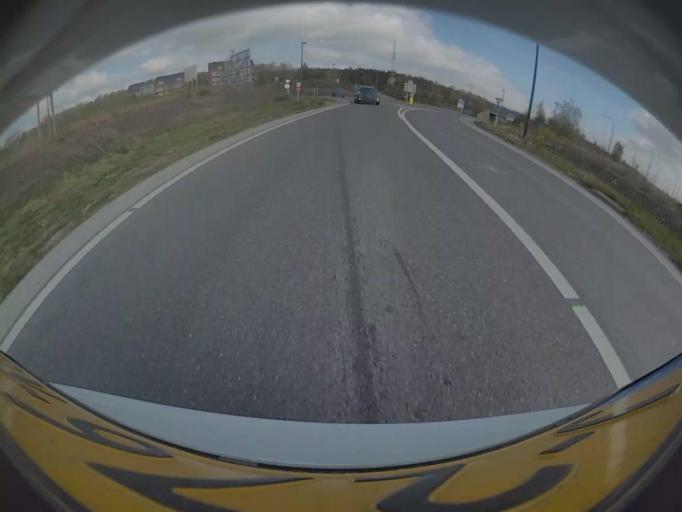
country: BE
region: Wallonia
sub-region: Province du Luxembourg
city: Marche-en-Famenne
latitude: 50.2318
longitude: 5.3093
